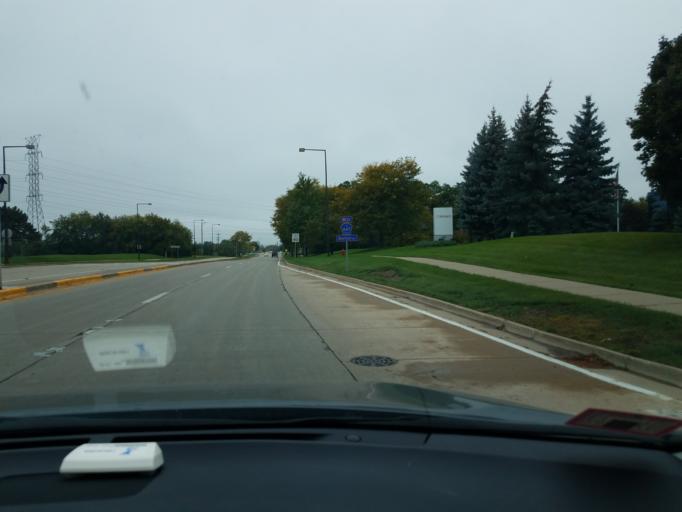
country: US
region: Illinois
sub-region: Cook County
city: Buffalo Grove
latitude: 42.1712
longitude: -87.9434
